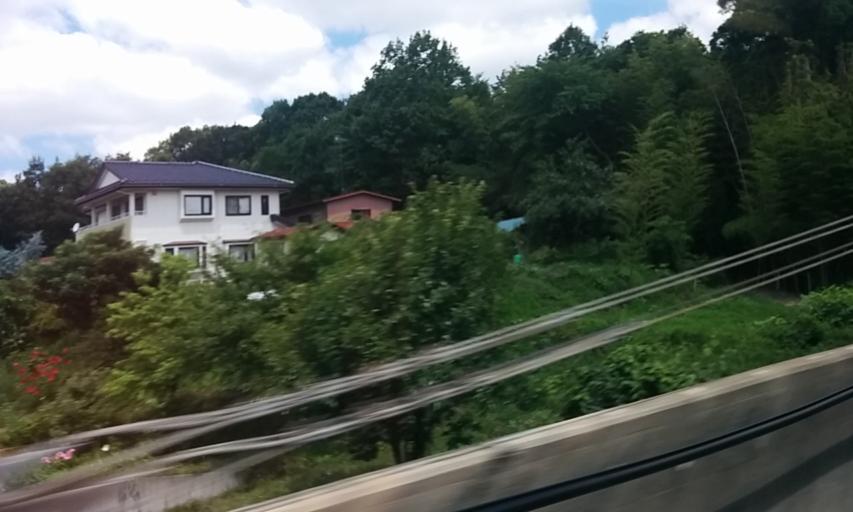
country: JP
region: Fukushima
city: Motomiya
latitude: 37.5066
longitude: 140.4280
